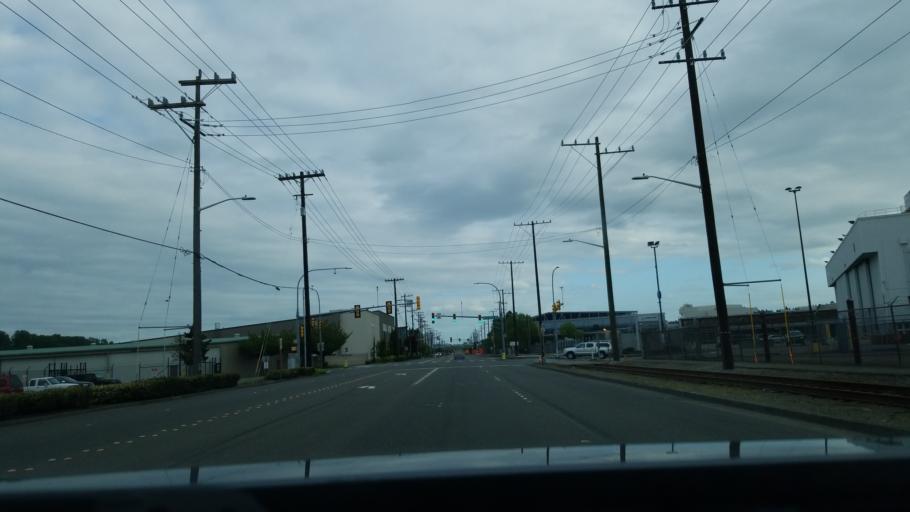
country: US
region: Washington
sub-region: King County
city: Boulevard Park
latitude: 47.5249
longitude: -122.3020
